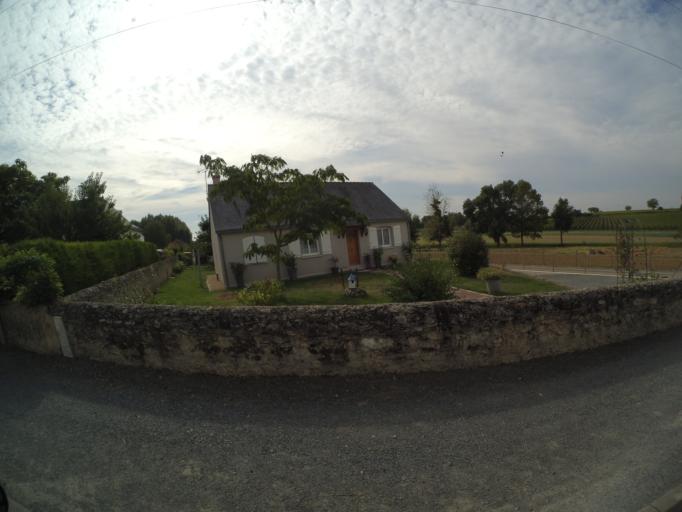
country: FR
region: Pays de la Loire
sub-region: Departement de Maine-et-Loire
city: Martigne-Briand
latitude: 47.2006
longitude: -0.4311
